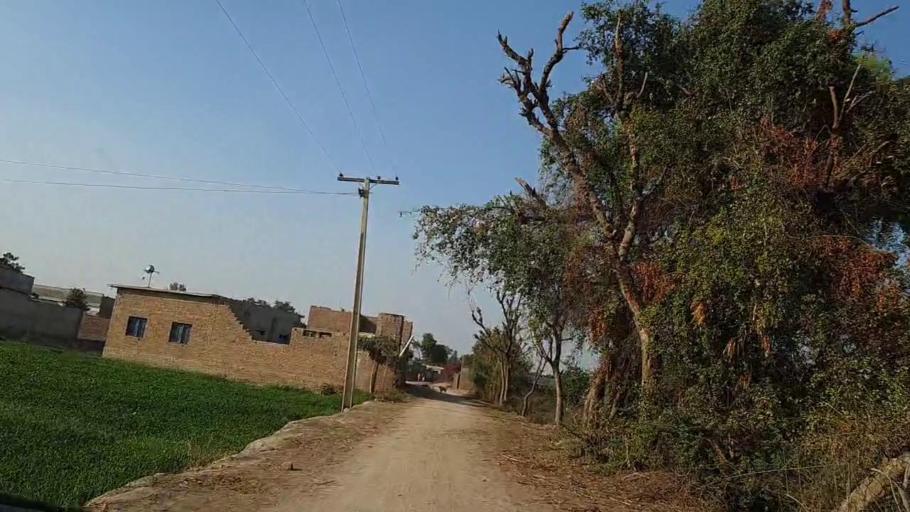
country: PK
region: Sindh
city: Sakrand
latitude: 26.1276
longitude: 68.2221
